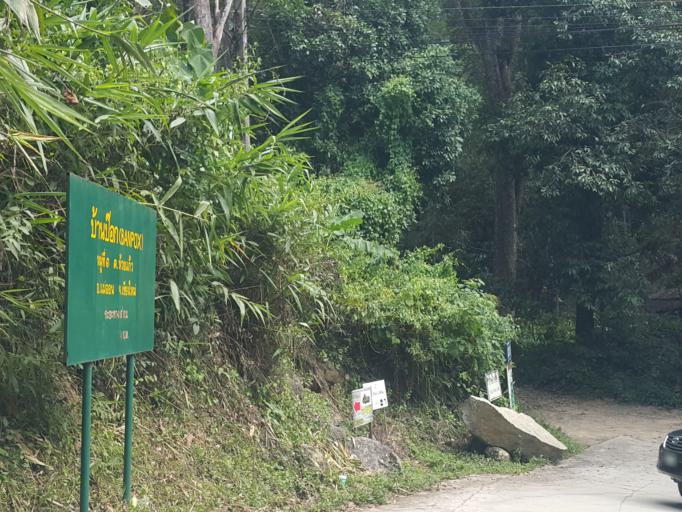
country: TH
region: Chiang Mai
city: Mae On
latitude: 18.8840
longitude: 99.3598
